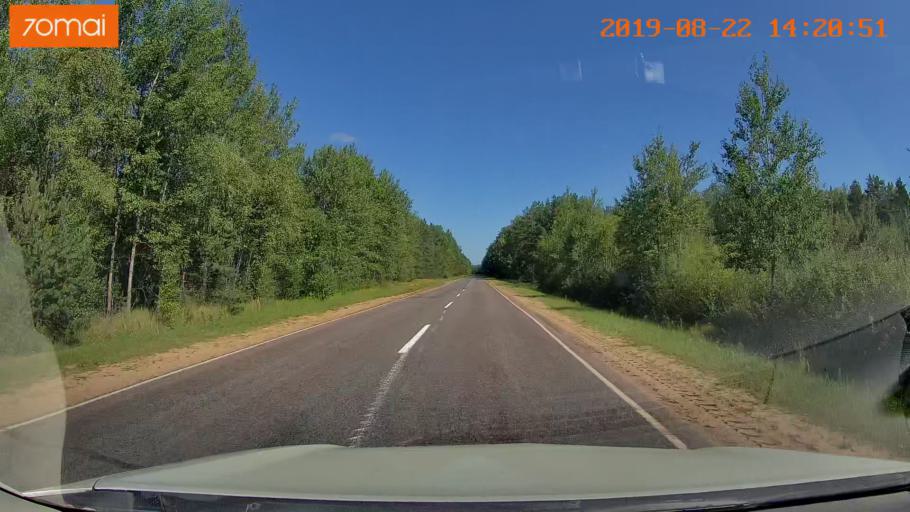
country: BY
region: Mogilev
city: Asipovichy
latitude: 53.2655
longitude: 28.5380
